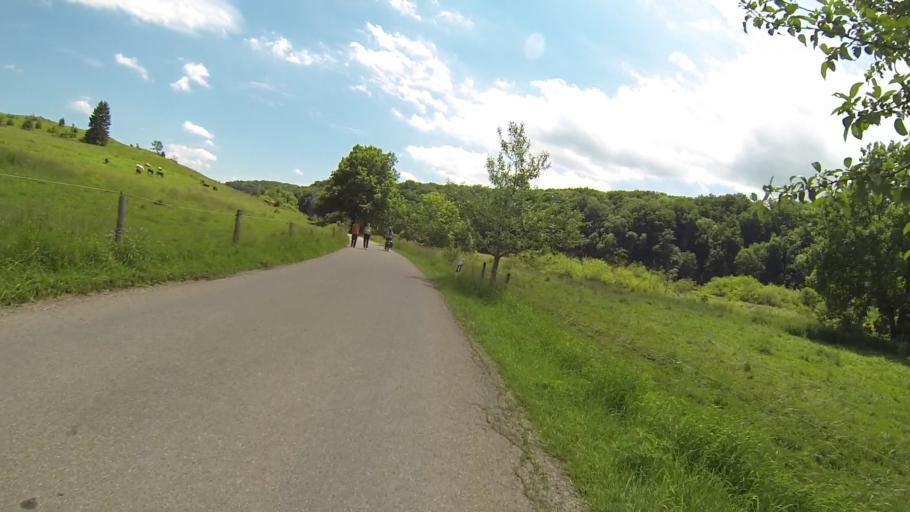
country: DE
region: Baden-Wuerttemberg
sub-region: Regierungsbezirk Stuttgart
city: Herbrechtingen
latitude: 48.6043
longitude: 10.1751
